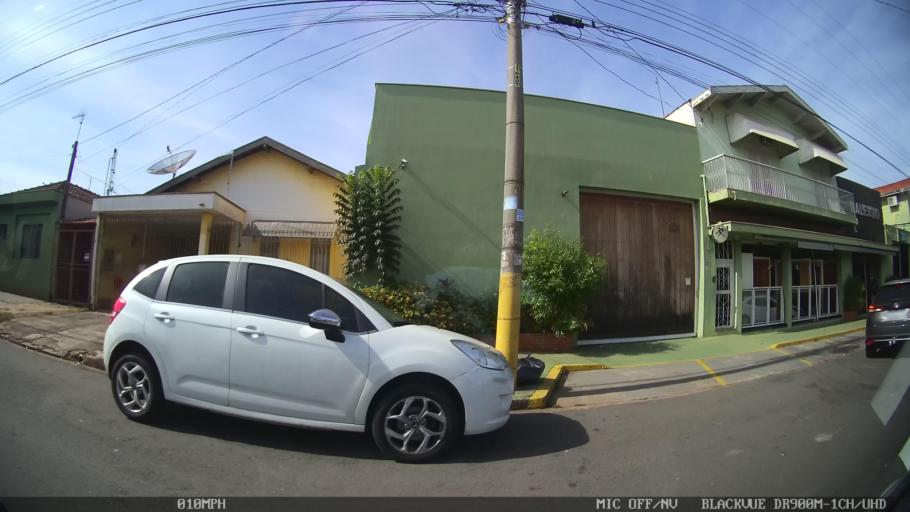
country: BR
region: Sao Paulo
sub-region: Piracicaba
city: Piracicaba
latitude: -22.7094
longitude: -47.6585
